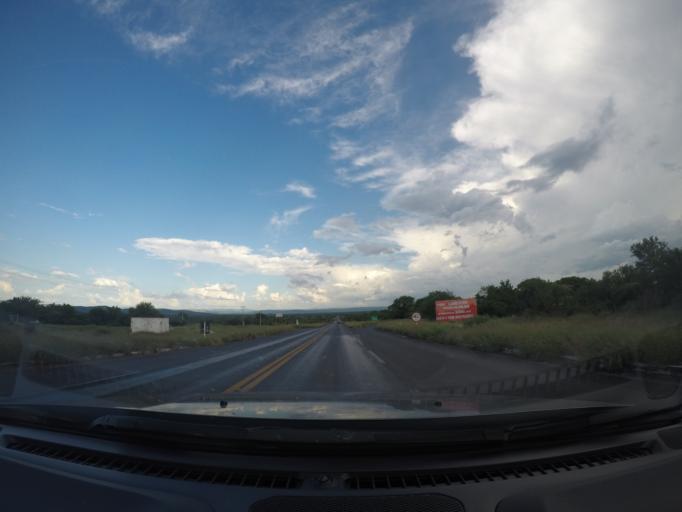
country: BR
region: Bahia
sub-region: Ibotirama
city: Ibotirama
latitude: -12.1313
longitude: -43.3391
